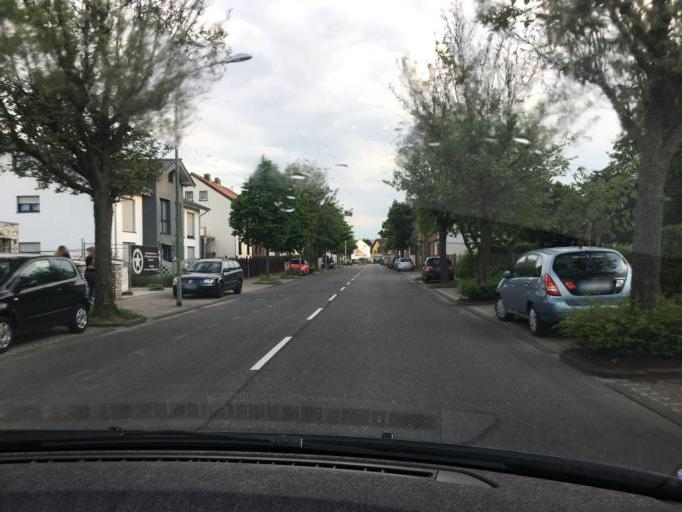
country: DE
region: North Rhine-Westphalia
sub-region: Regierungsbezirk Koln
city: Dueren
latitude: 50.8308
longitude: 6.4570
